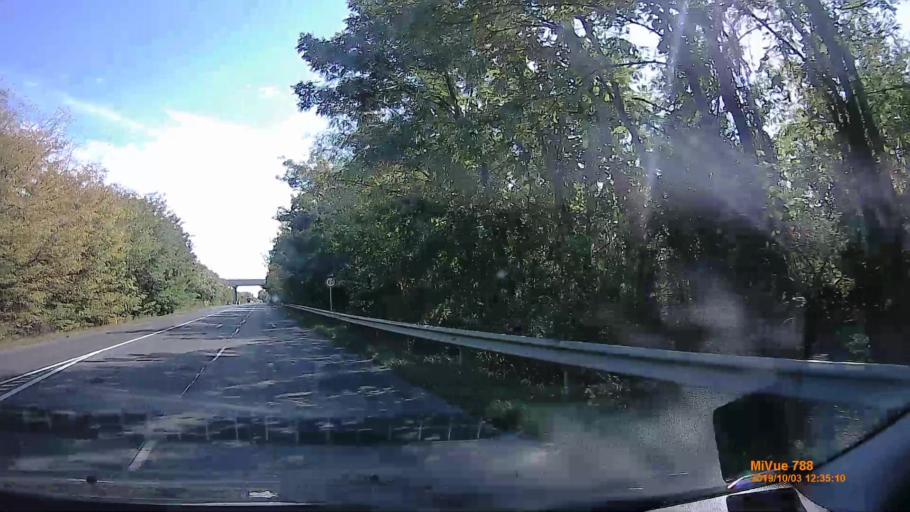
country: HU
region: Pest
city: Szod
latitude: 47.7476
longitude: 19.1733
